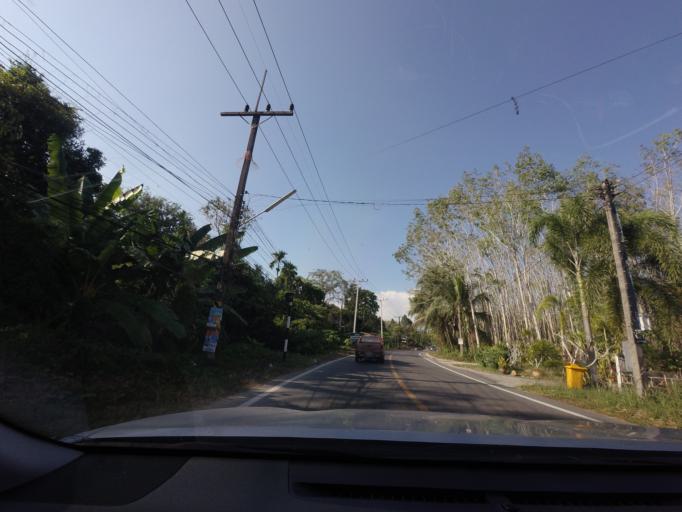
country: TH
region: Phangnga
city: Takua Thung
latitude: 8.2737
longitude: 98.3715
